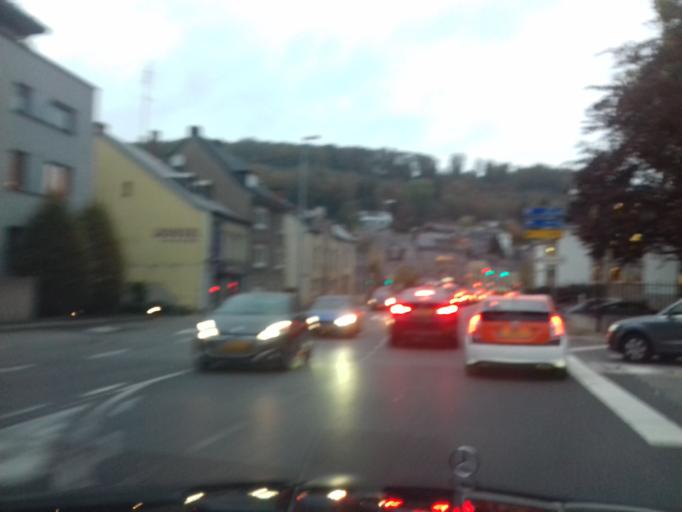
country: LU
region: Luxembourg
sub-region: Canton de Luxembourg
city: Luxembourg
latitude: 49.6271
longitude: 6.1298
